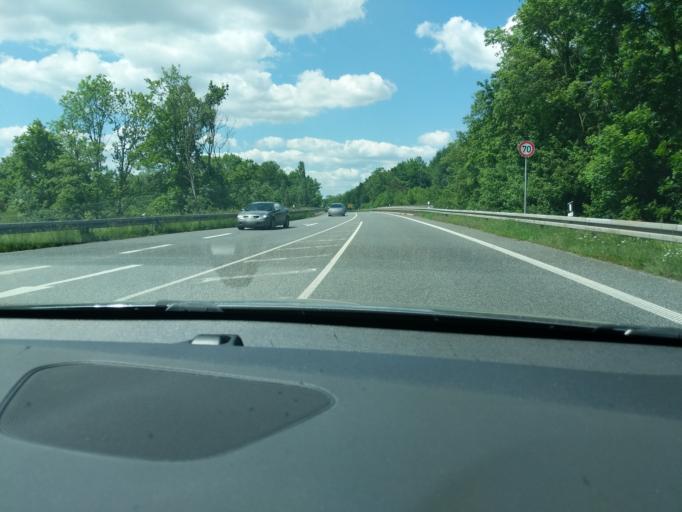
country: DE
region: Hesse
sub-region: Regierungsbezirk Darmstadt
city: Maintal
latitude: 50.1475
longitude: 8.8284
